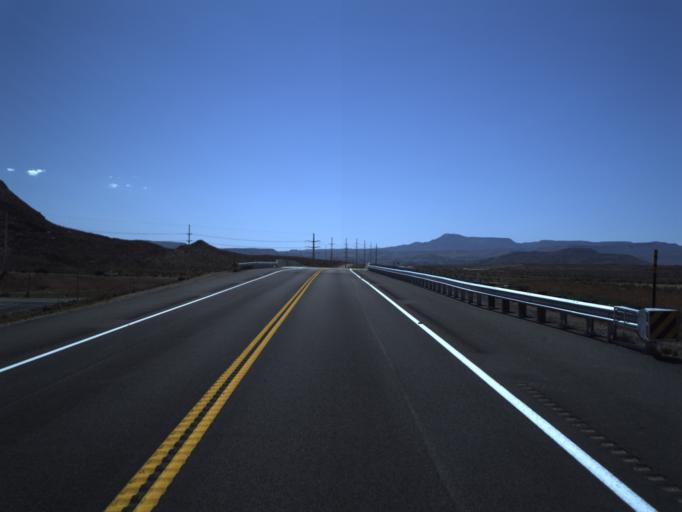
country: US
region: Utah
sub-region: Washington County
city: Washington
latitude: 37.0607
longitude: -113.4860
